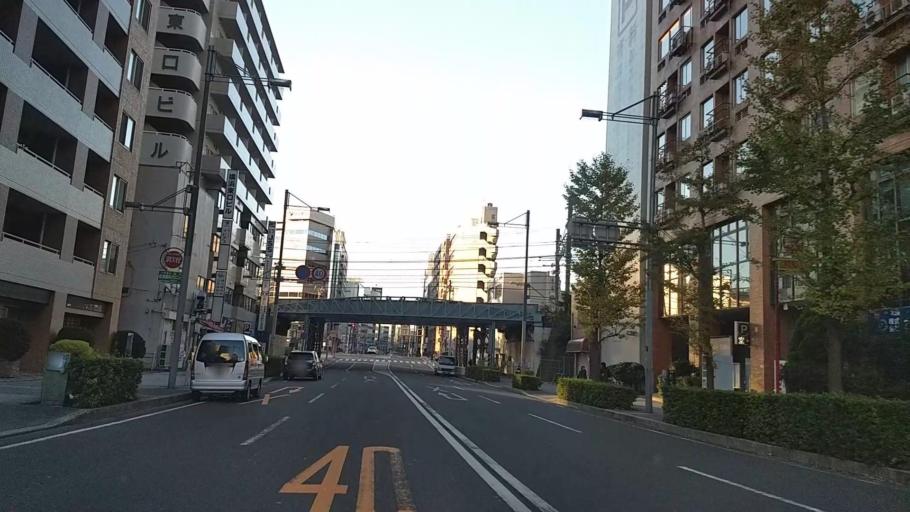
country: JP
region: Kanagawa
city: Yokohama
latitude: 35.4626
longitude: 139.6221
